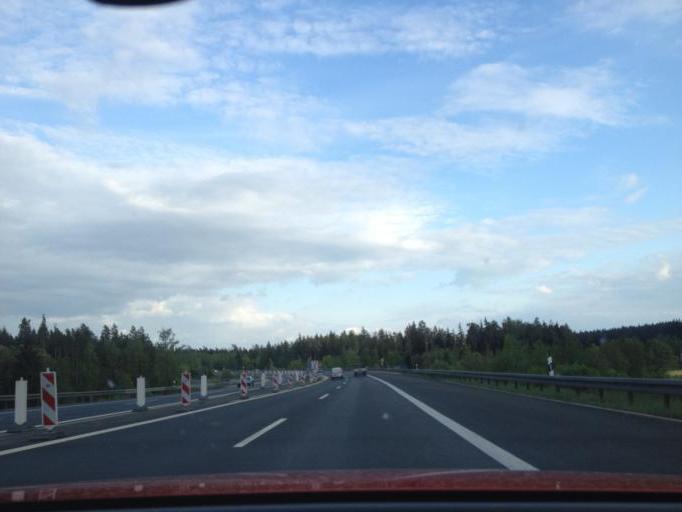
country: DE
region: Bavaria
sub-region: Upper Palatinate
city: Pechbrunn
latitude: 49.9578
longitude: 12.1921
